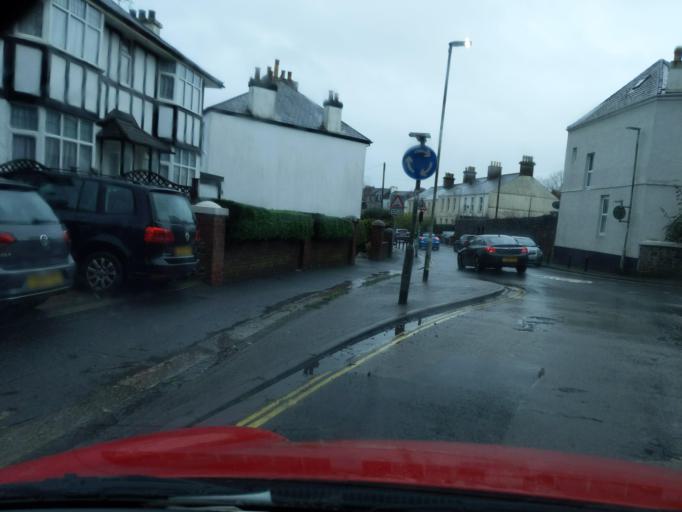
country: GB
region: England
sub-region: Plymouth
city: Plymouth
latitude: 50.3929
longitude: -4.1274
